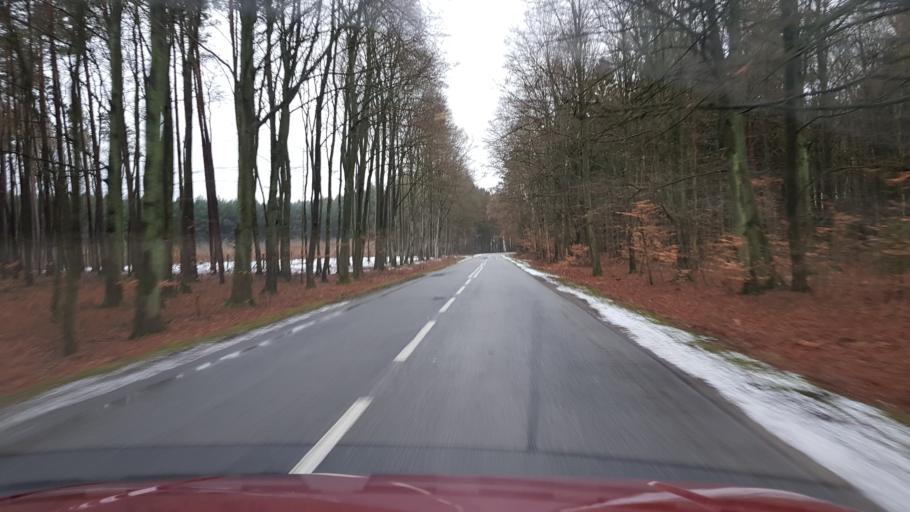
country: PL
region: West Pomeranian Voivodeship
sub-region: Powiat gryficki
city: Ploty
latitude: 53.7153
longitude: 15.2933
